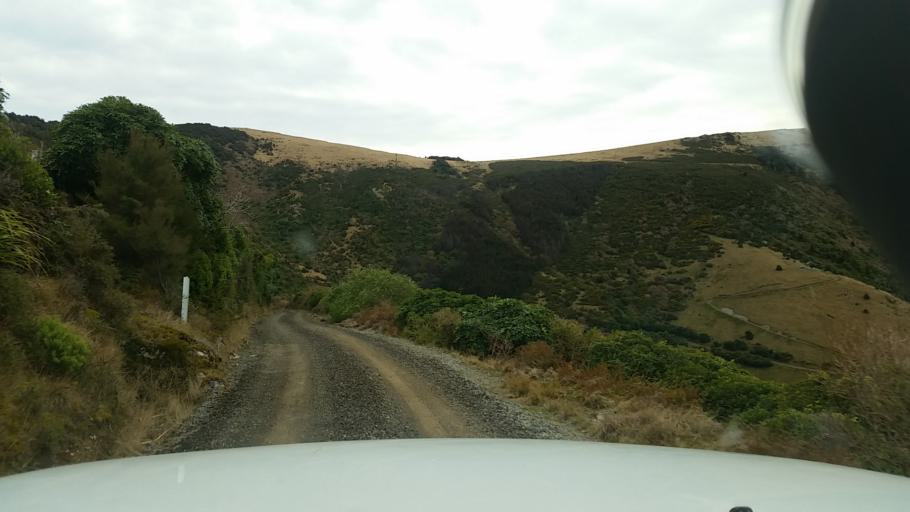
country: NZ
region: Canterbury
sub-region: Christchurch City
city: Christchurch
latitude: -43.7228
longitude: 172.7885
